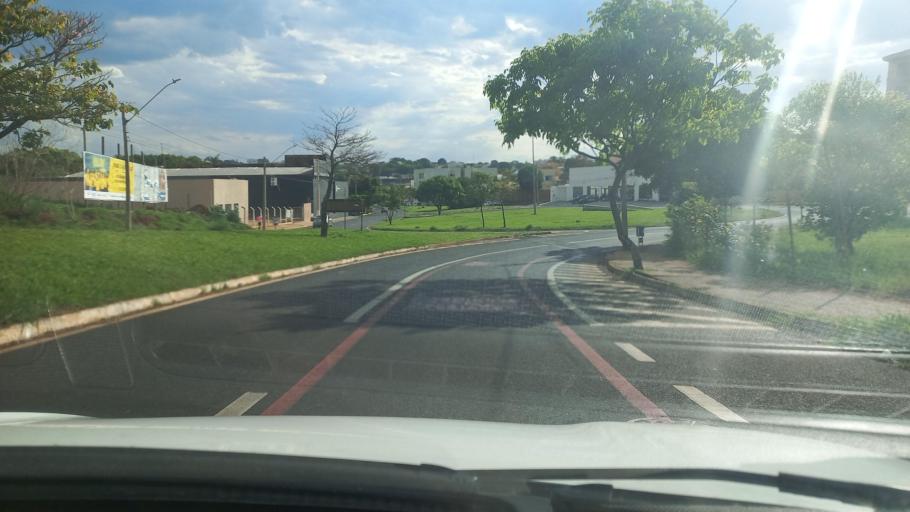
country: BR
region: Minas Gerais
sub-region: Uberaba
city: Uberaba
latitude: -19.7531
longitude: -47.9139
